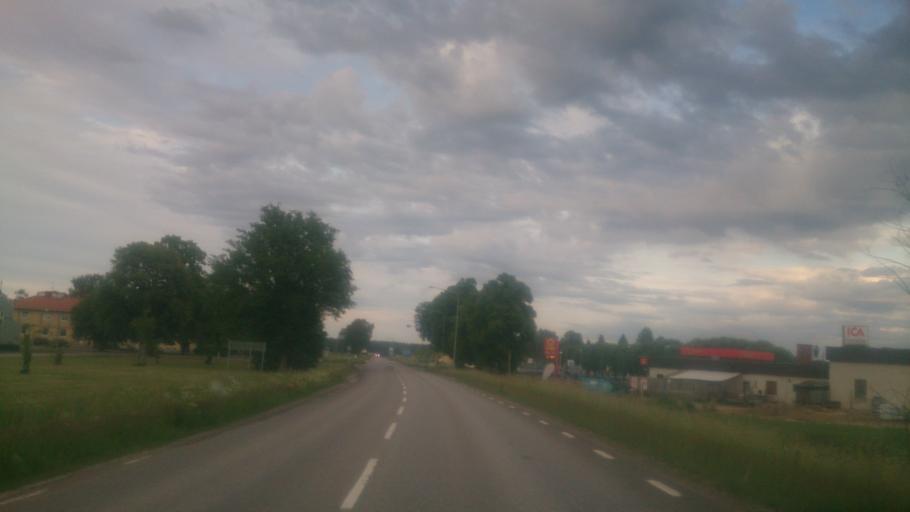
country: SE
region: OEstergoetland
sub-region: Motala Kommun
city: Borensberg
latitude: 58.4786
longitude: 15.2239
